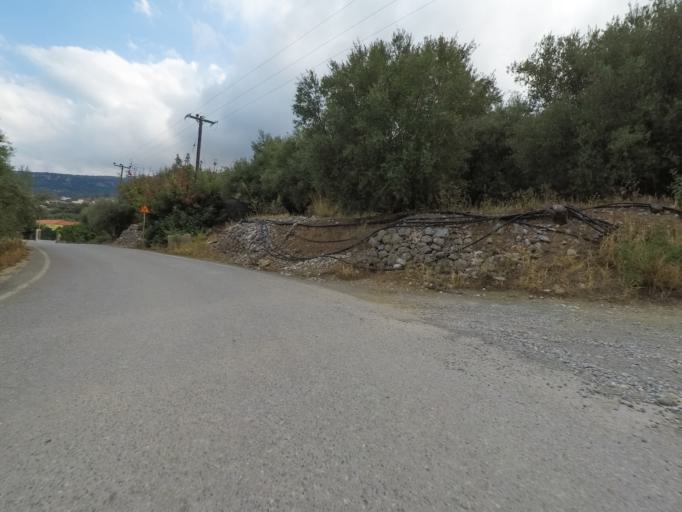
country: GR
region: Crete
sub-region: Nomos Lasithiou
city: Kritsa
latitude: 35.1608
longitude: 25.6480
